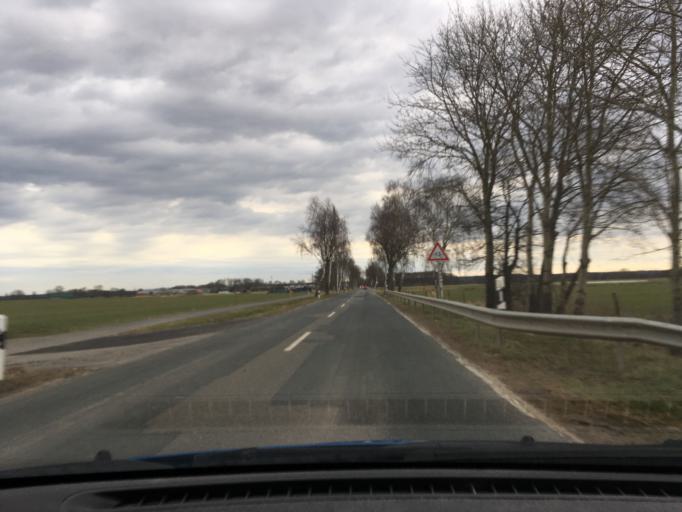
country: DE
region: Lower Saxony
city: Handorf
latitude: 53.3717
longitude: 10.3387
